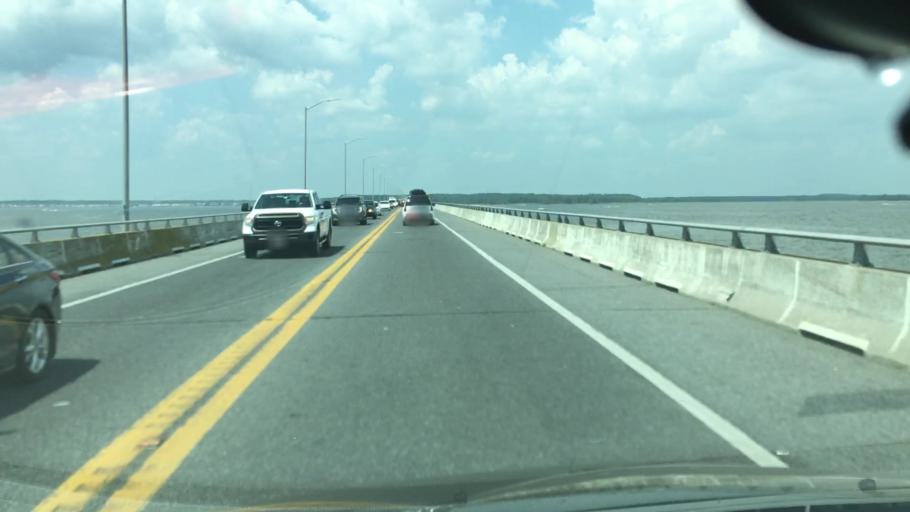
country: US
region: Maryland
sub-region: Worcester County
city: Ocean City
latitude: 38.3869
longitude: -75.0786
